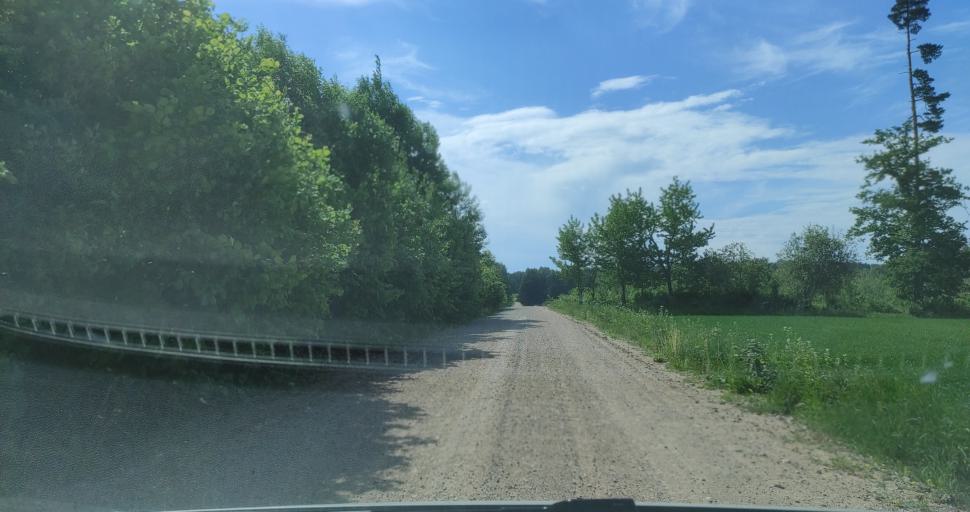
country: LV
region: Kuldigas Rajons
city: Kuldiga
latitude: 56.8475
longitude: 21.9405
